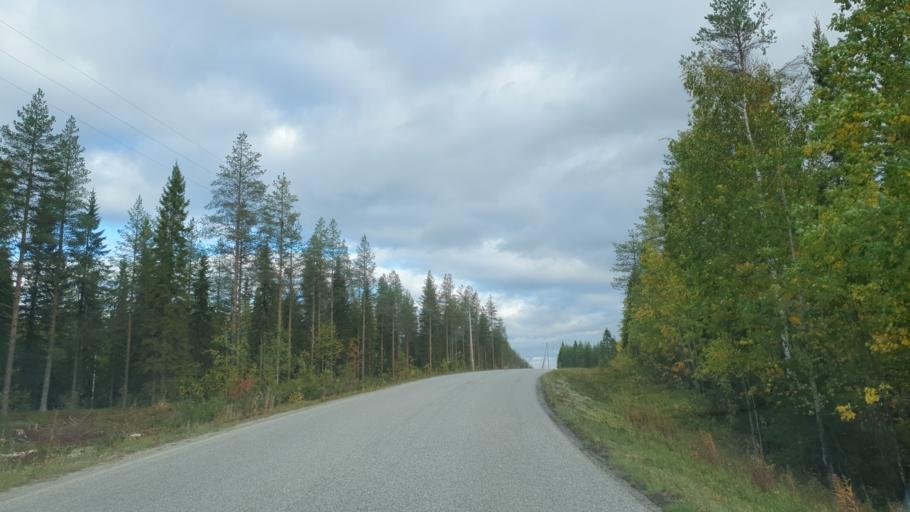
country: FI
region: Kainuu
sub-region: Kehys-Kainuu
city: Kuhmo
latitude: 63.9519
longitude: 29.8351
